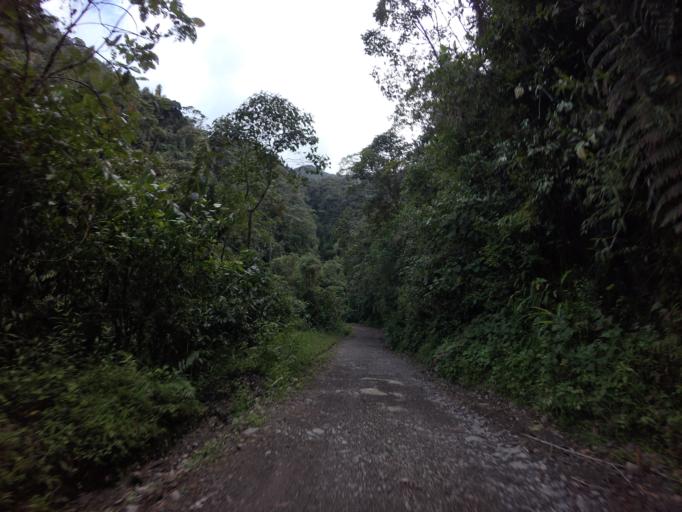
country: CO
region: Caldas
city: Pensilvania
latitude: 5.4509
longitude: -75.1570
